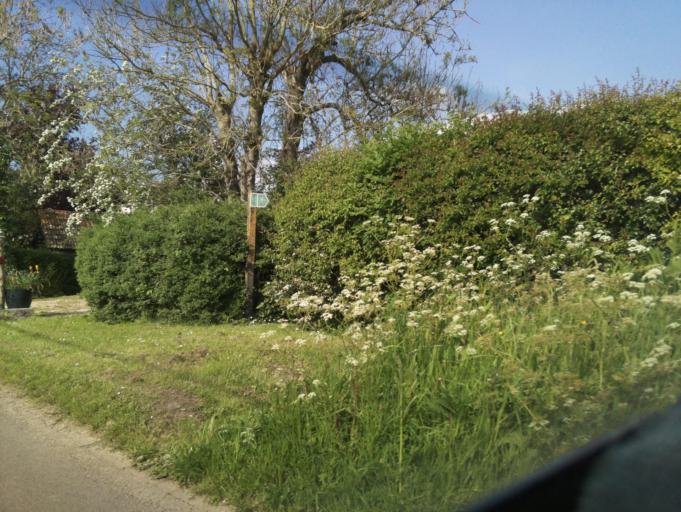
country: GB
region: England
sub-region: Wiltshire
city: Malmesbury
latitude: 51.5341
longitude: -2.0798
